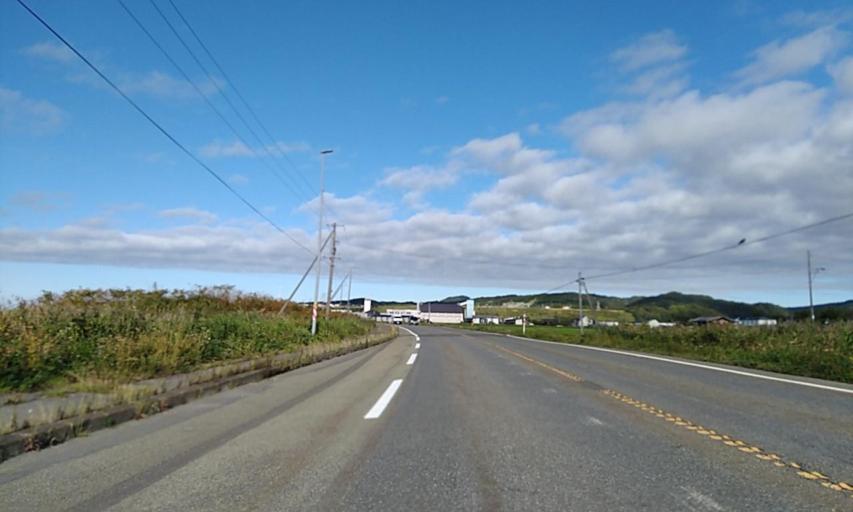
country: JP
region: Hokkaido
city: Shizunai-furukawacho
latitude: 42.2439
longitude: 142.5862
